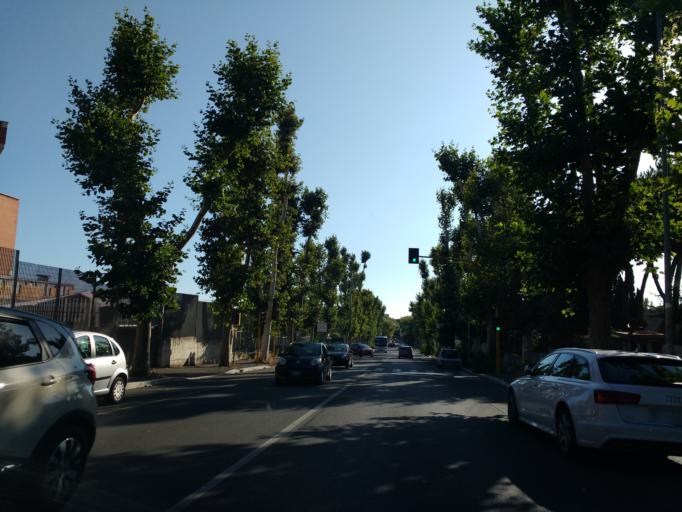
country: IT
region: Latium
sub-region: Citta metropolitana di Roma Capitale
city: Acilia-Castel Fusano-Ostia Antica
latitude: 41.7794
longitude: 12.3597
